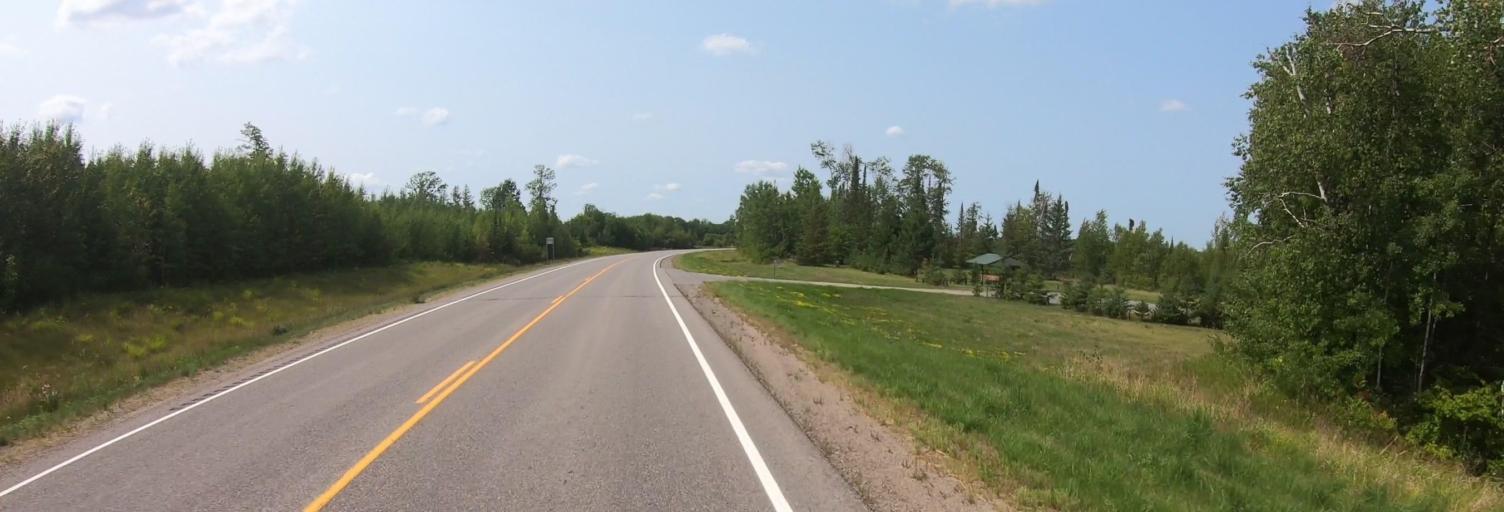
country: US
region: Minnesota
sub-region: Lake of the Woods County
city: Baudette
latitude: 48.6435
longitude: -94.1524
